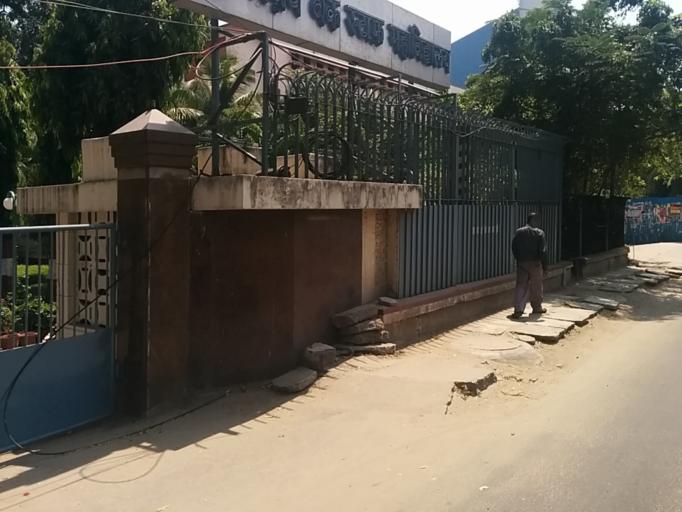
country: IN
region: Tamil Nadu
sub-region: Chennai
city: Chetput
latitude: 13.0449
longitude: 80.2482
